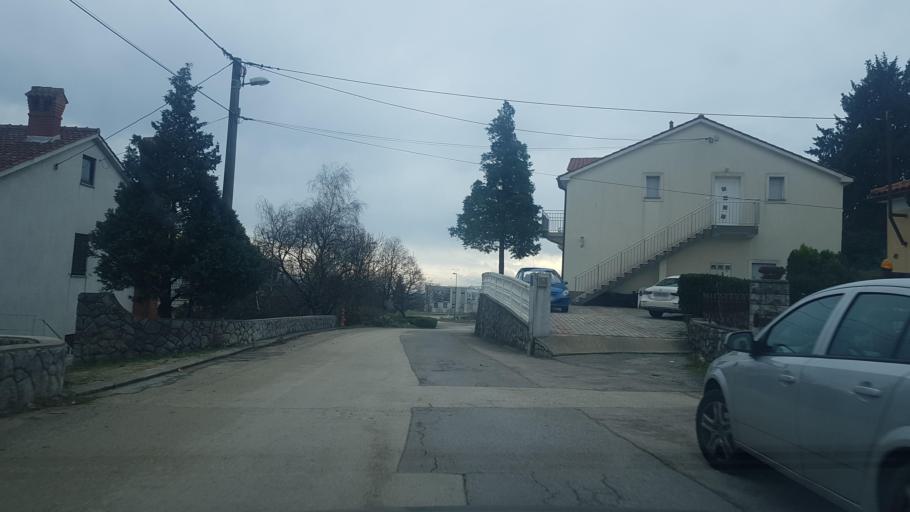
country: HR
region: Primorsko-Goranska
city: Matulji
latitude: 45.3751
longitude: 14.3195
